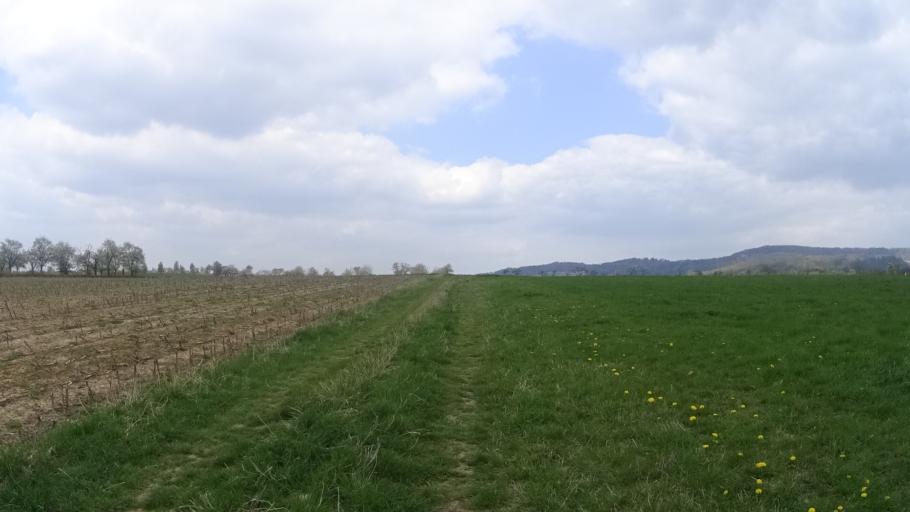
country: DE
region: Bavaria
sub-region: Upper Franconia
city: Kleinsendelbach
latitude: 49.6035
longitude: 11.1799
